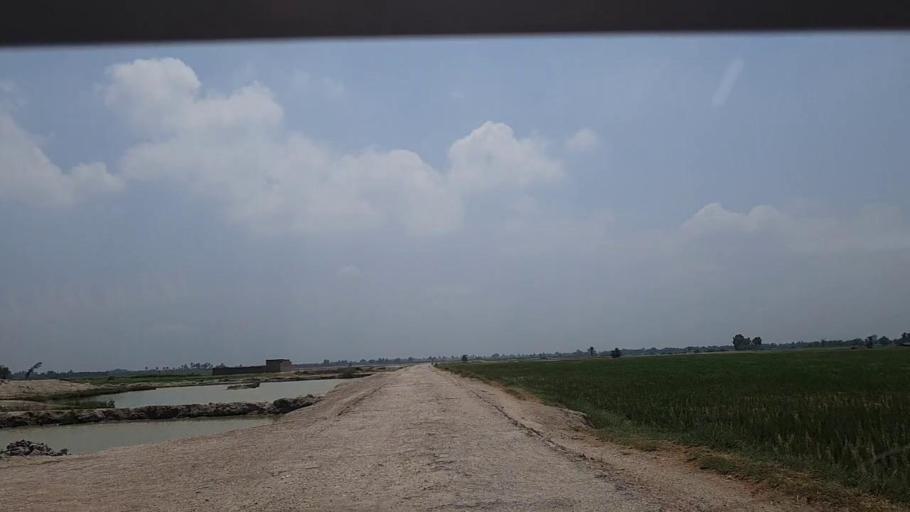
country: PK
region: Sindh
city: Khanpur
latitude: 27.9022
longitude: 69.3913
